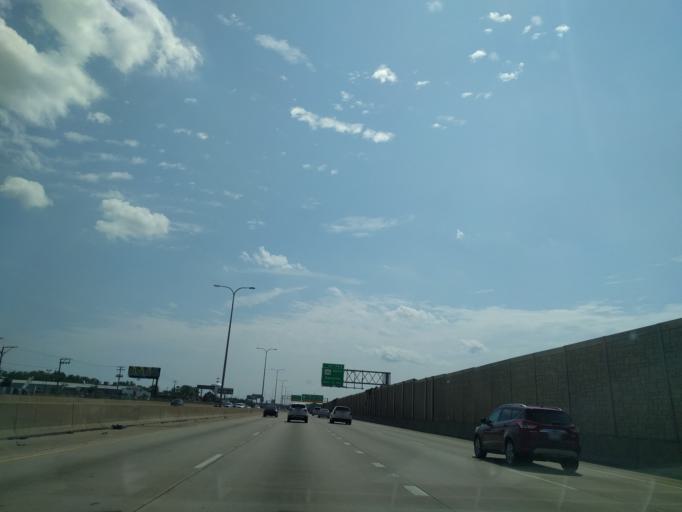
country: US
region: Illinois
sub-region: Cook County
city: South Holland
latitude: 41.5956
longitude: -87.5837
